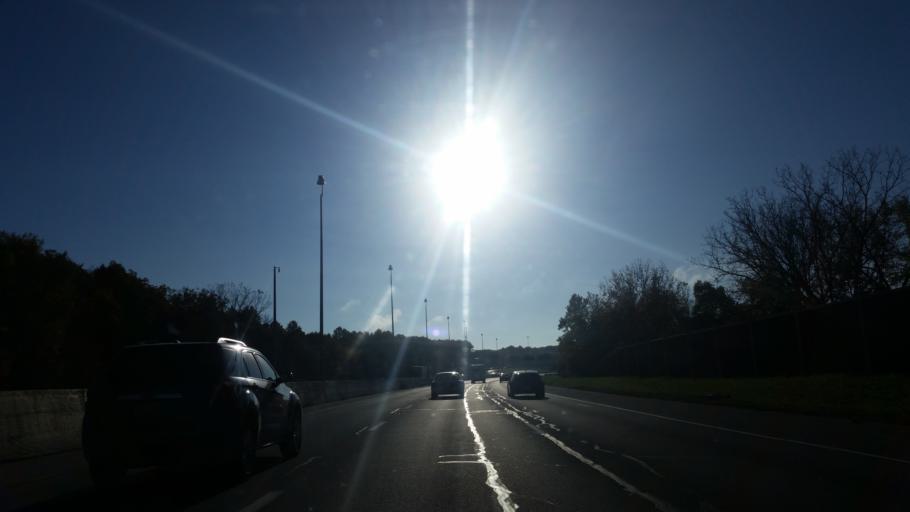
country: US
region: Ohio
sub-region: Summit County
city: Fairlawn
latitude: 41.1175
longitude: -81.6178
